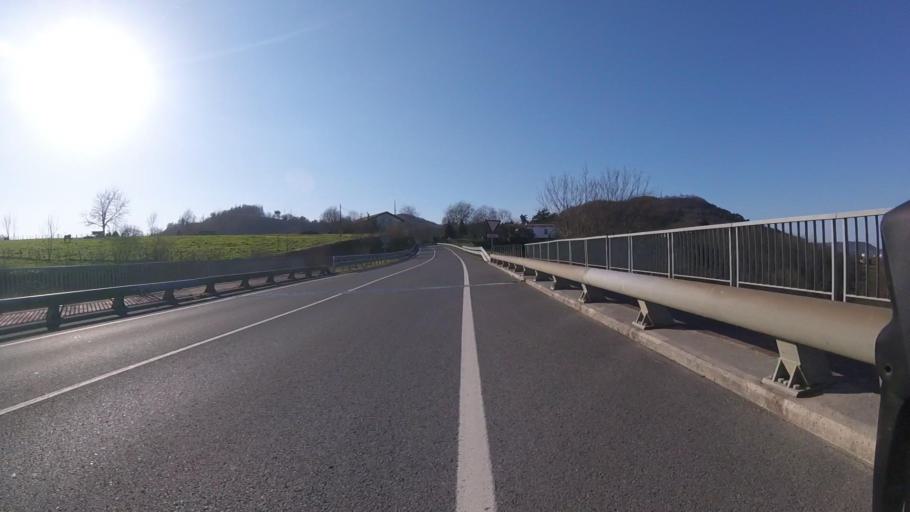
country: ES
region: Basque Country
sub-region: Provincia de Guipuzcoa
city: Errenteria
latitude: 43.2917
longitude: -1.9023
